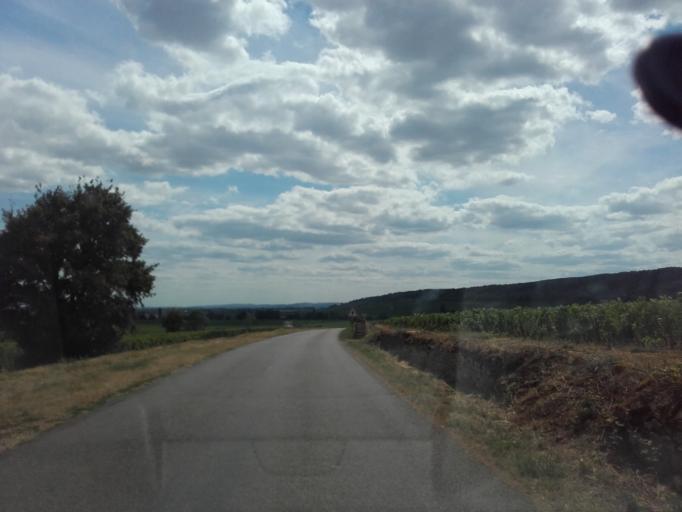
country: FR
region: Bourgogne
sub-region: Departement de la Cote-d'Or
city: Savigny-les-Beaune
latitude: 47.0648
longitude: 4.8448
